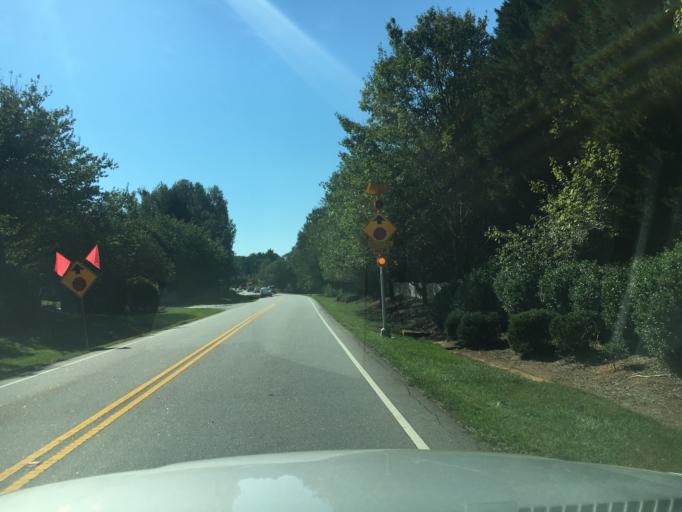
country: US
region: South Carolina
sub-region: Greenville County
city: Taylors
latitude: 34.8784
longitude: -82.2831
